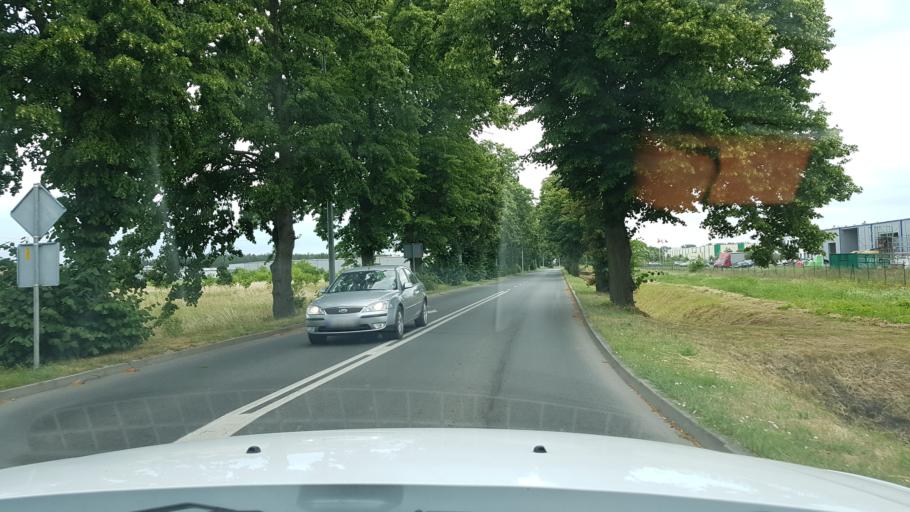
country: PL
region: Lubusz
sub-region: Powiat gorzowski
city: Kostrzyn nad Odra
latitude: 52.6078
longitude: 14.6184
